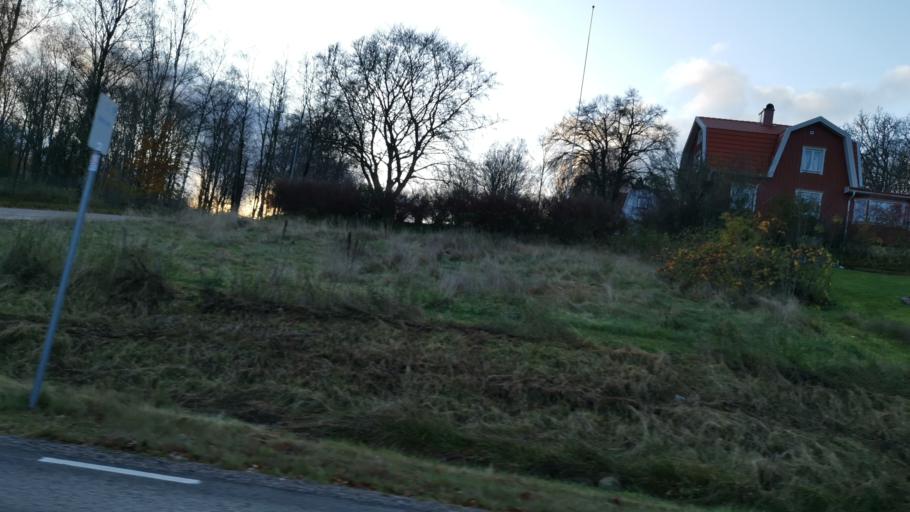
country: SE
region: Vaestra Goetaland
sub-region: Munkedals Kommun
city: Munkedal
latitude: 58.4873
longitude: 11.6938
